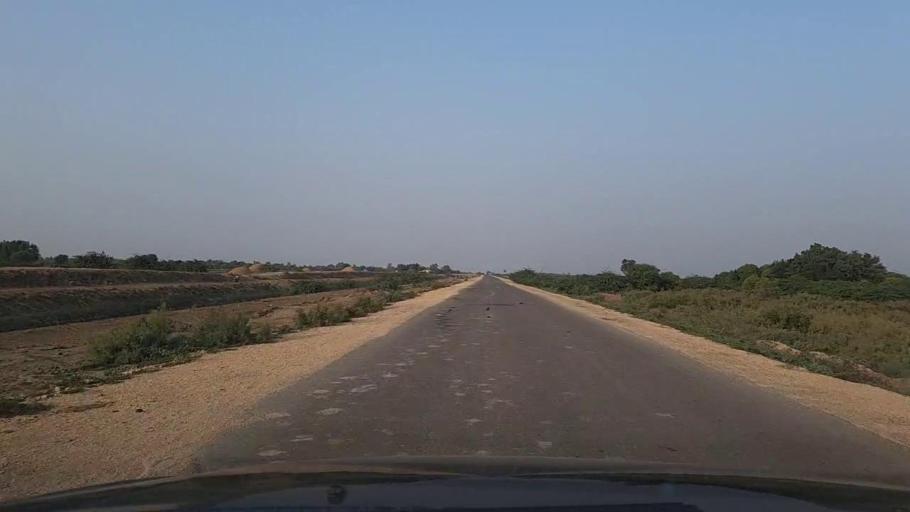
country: PK
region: Sindh
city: Mirpur Sakro
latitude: 24.4808
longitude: 67.8049
